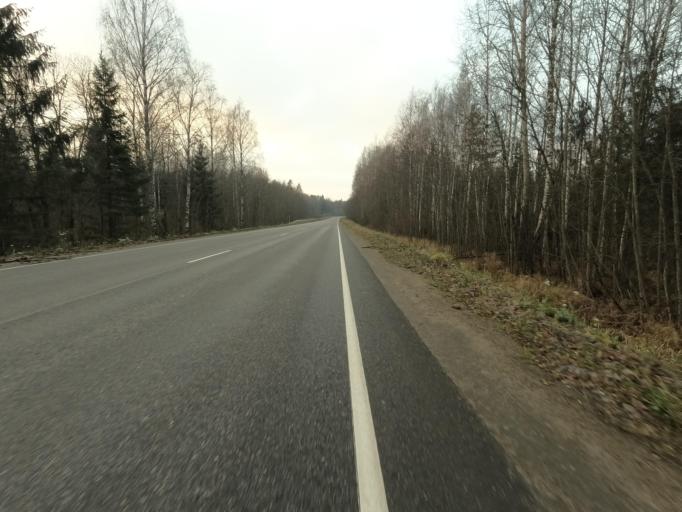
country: RU
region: Leningrad
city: Kirovsk
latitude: 59.8167
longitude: 30.9703
